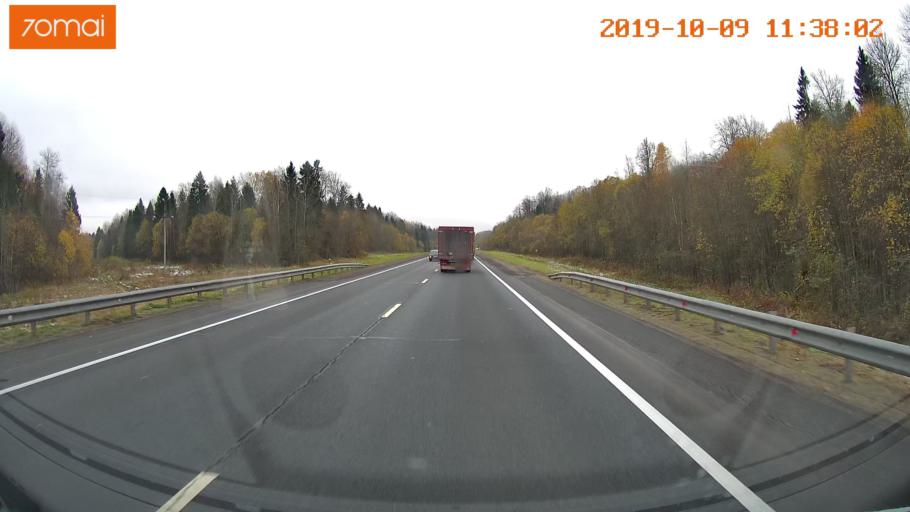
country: RU
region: Vologda
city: Gryazovets
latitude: 58.9725
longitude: 40.1522
